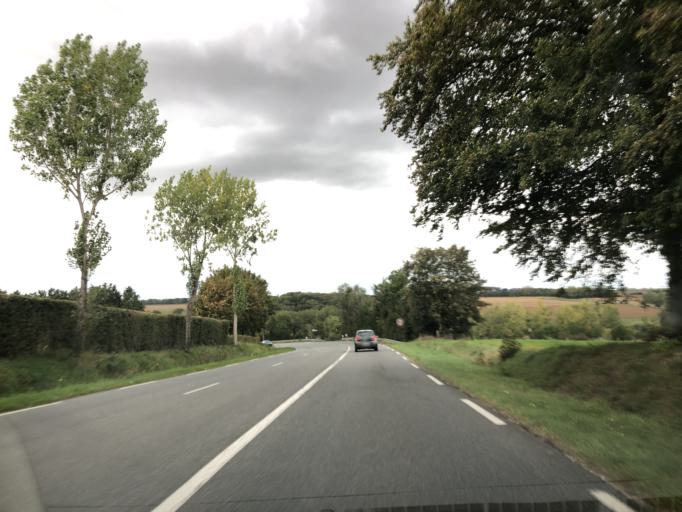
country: FR
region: Picardie
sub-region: Departement de la Somme
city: Chepy
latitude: 50.1001
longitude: 1.7266
